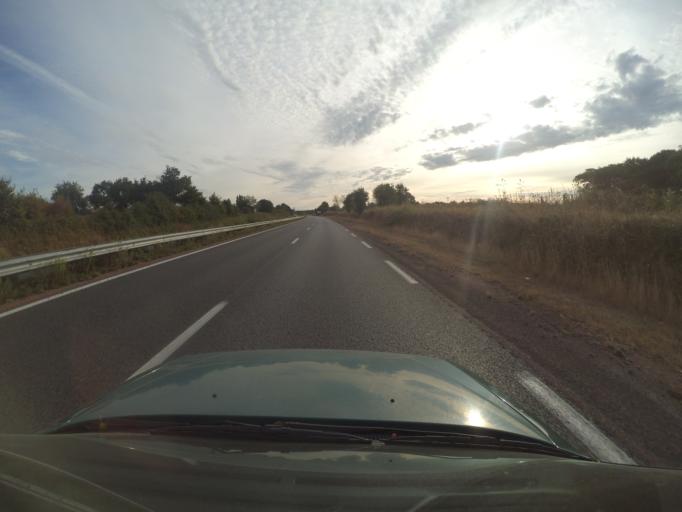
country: FR
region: Pays de la Loire
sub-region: Departement de la Vendee
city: Saint-Andre-Treize-Voies
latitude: 46.9159
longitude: -1.3792
